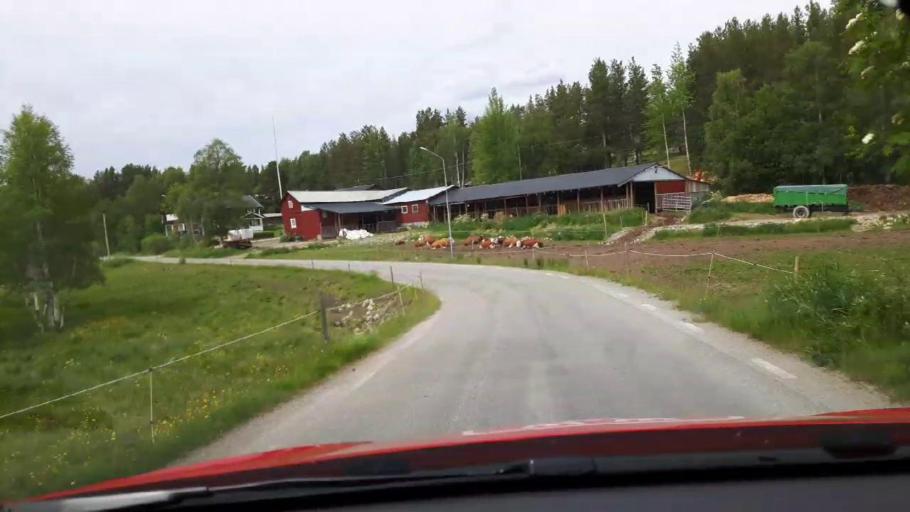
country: SE
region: Jaemtland
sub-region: Harjedalens Kommun
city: Sveg
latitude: 62.4107
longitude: 13.6705
